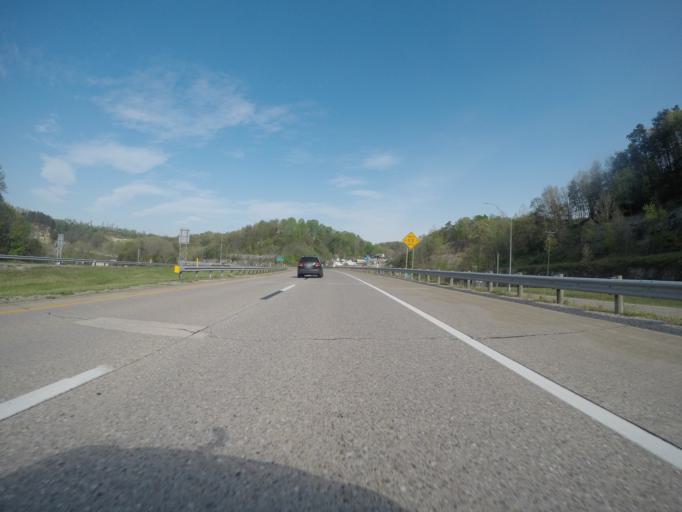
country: US
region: West Virginia
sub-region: Kanawha County
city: South Charleston
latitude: 38.3411
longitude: -81.7001
